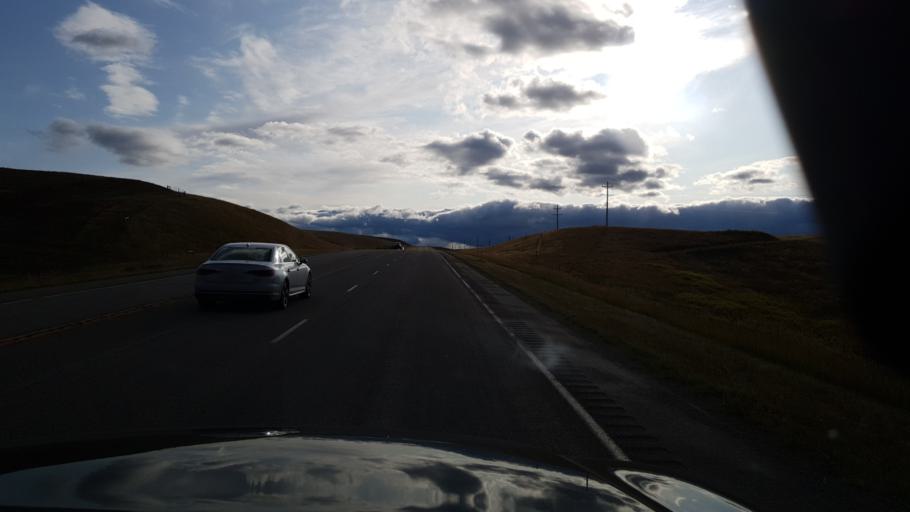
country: US
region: Montana
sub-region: Glacier County
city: South Browning
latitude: 48.5200
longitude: -113.0762
